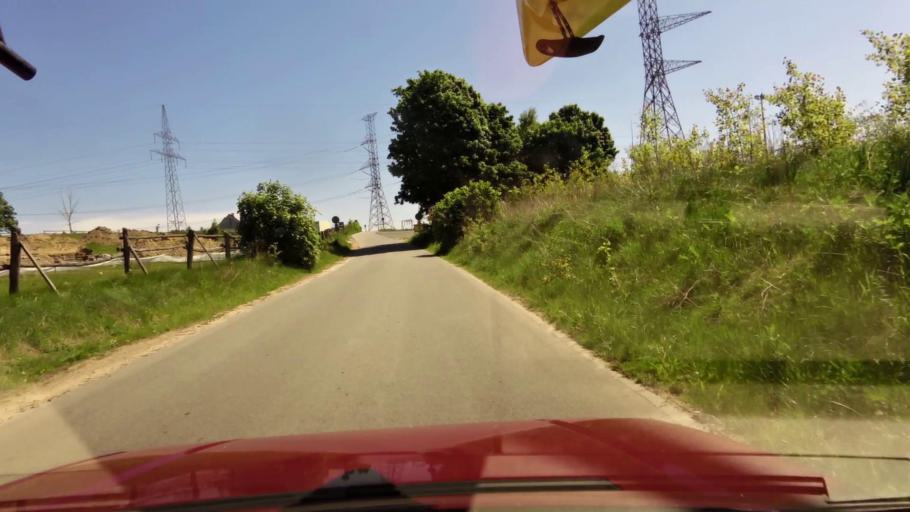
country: PL
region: West Pomeranian Voivodeship
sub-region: Powiat koszalinski
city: Polanow
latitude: 54.0437
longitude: 16.7279
